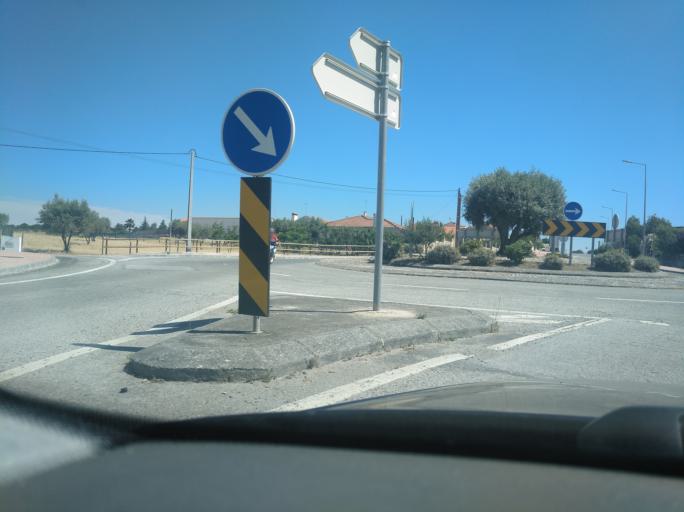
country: PT
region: Beja
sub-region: Castro Verde
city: Castro Verde
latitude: 37.6067
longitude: -8.0813
